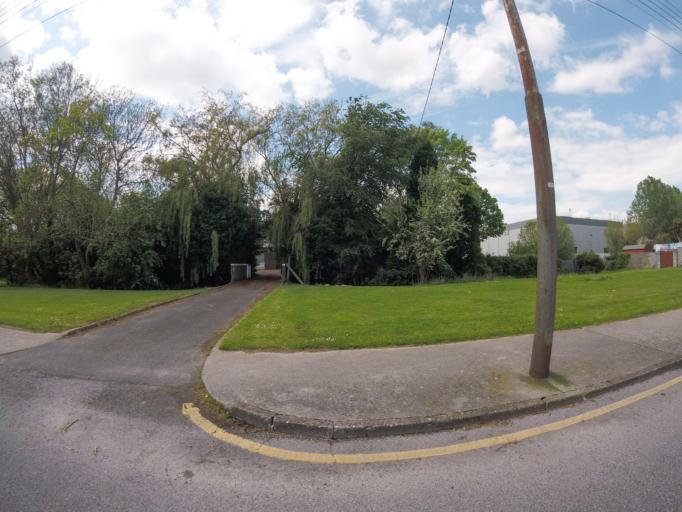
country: IE
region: Munster
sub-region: Waterford
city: Waterford
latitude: 52.2494
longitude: -7.1440
